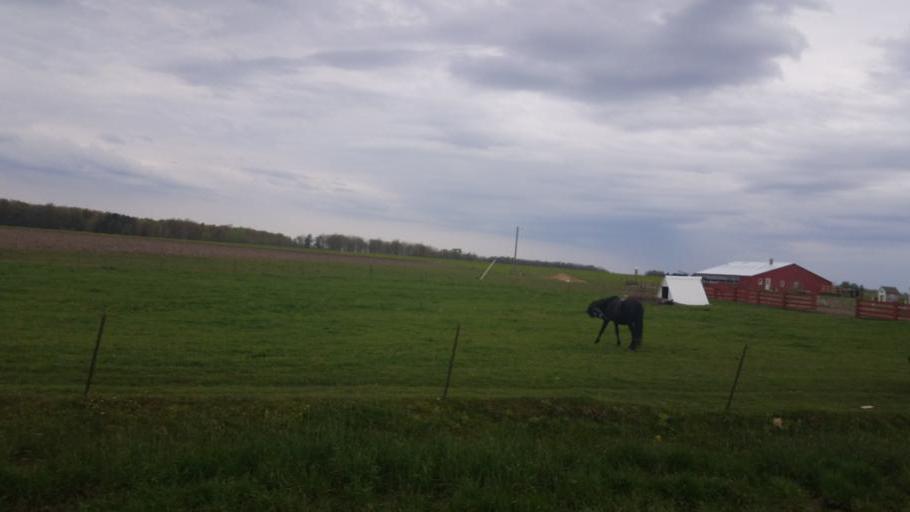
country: US
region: Wisconsin
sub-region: Marathon County
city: Spencer
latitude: 44.6491
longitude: -90.3772
